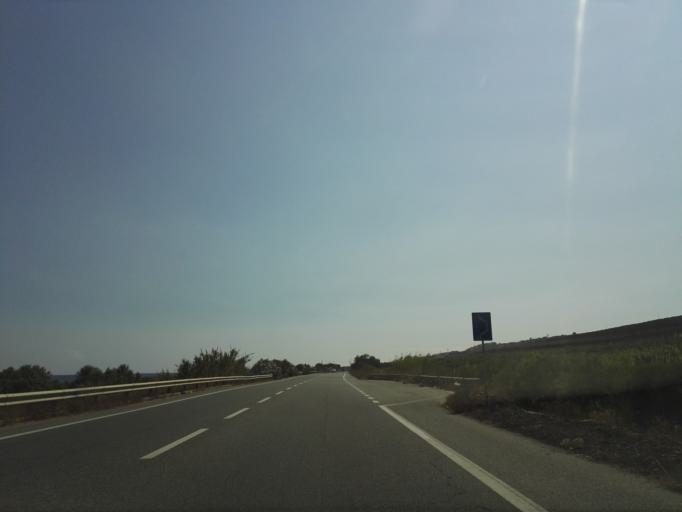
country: IT
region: Calabria
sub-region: Provincia di Reggio Calabria
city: Monasterace Marina
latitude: 38.4120
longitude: 16.5553
